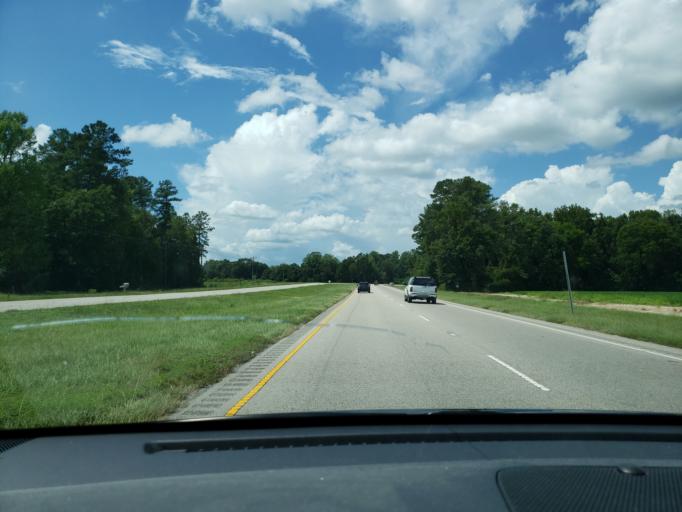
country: US
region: North Carolina
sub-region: Bladen County
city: Elizabethtown
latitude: 34.7226
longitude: -78.7618
